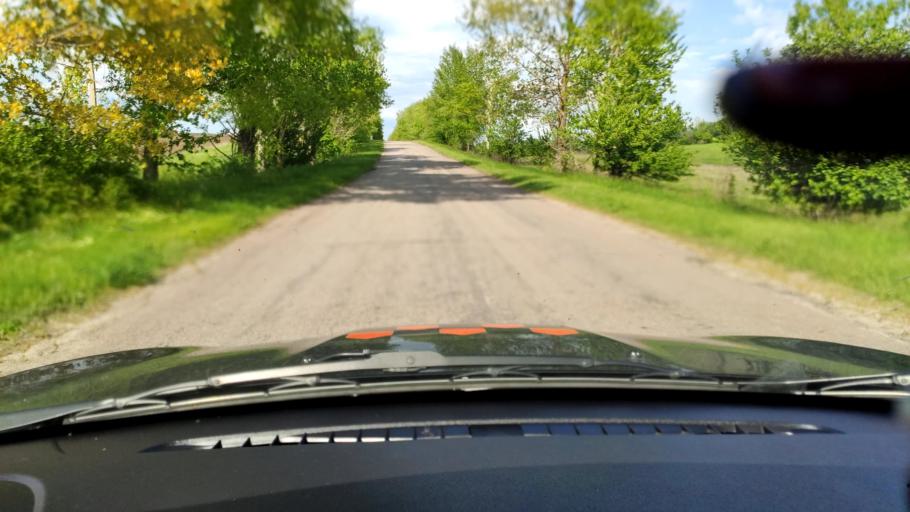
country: RU
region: Voronezj
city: Uryv-Pokrovka
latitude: 51.2004
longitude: 39.0626
